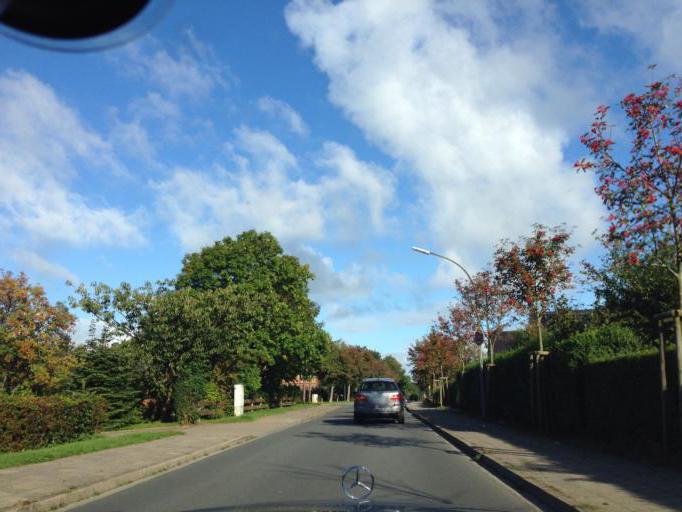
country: DE
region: Schleswig-Holstein
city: Wyk auf Fohr
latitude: 54.6898
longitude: 8.5599
